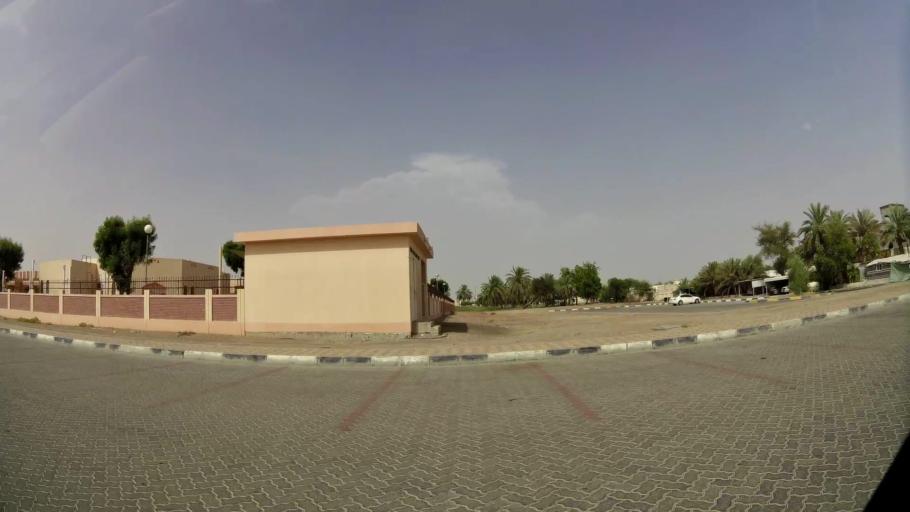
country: AE
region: Abu Dhabi
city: Al Ain
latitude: 24.1904
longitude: 55.6326
